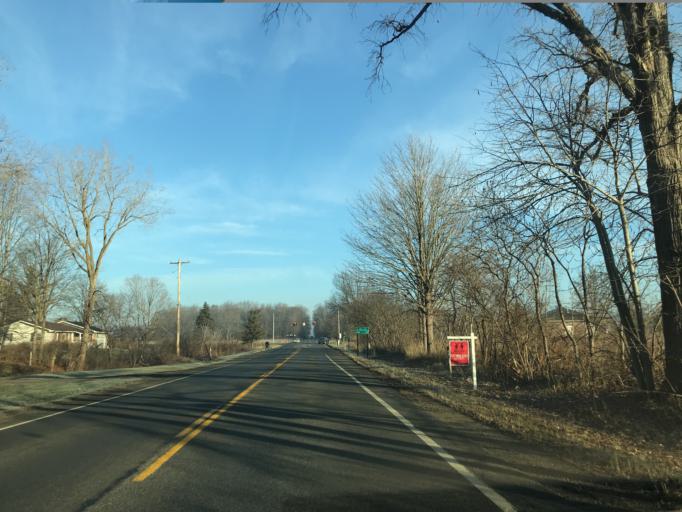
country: US
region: Michigan
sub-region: Eaton County
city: Dimondale
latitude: 42.6385
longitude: -84.6029
